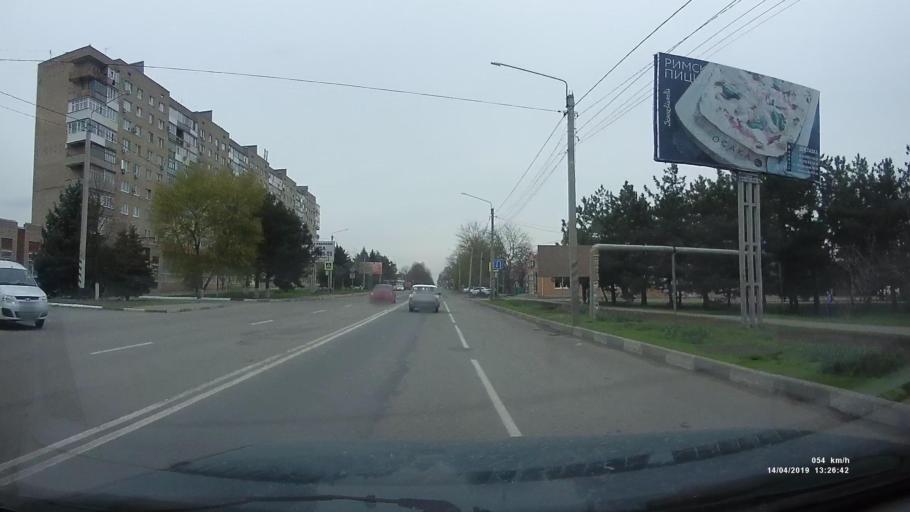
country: RU
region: Rostov
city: Azov
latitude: 47.0916
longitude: 39.4520
